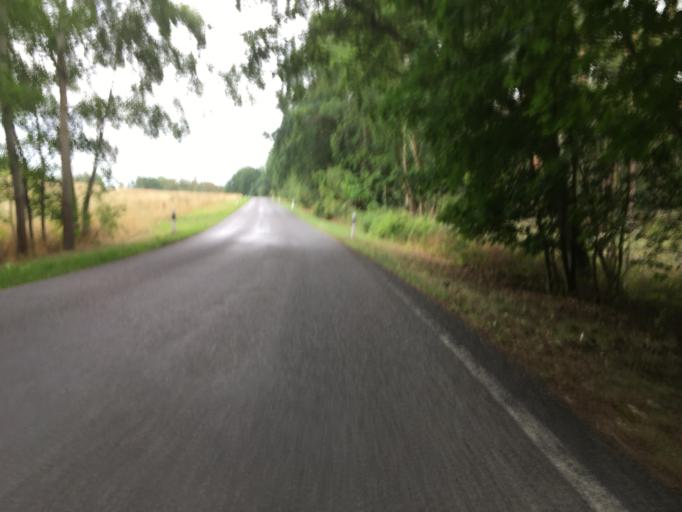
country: DE
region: Brandenburg
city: Gramzow
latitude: 53.2044
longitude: 13.9531
